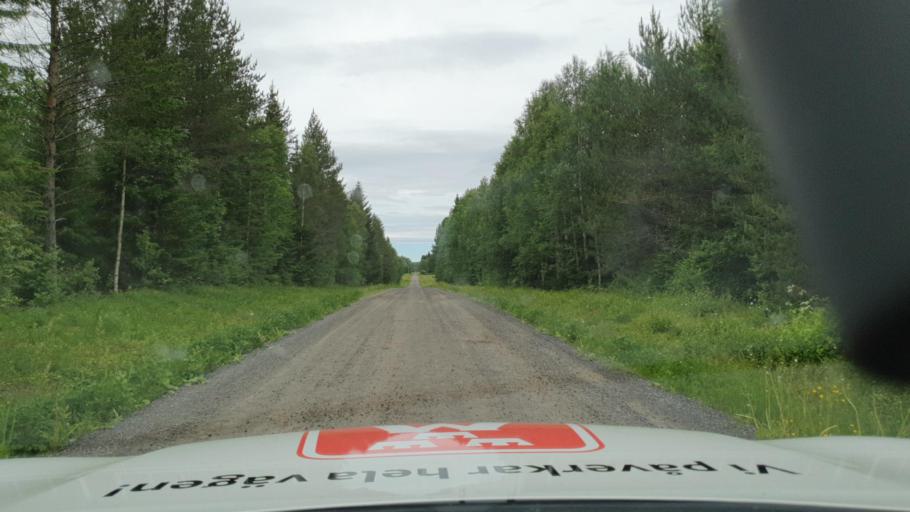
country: SE
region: Vaesterbotten
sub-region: Skelleftea Kommun
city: Burtraesk
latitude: 64.3952
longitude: 20.5855
